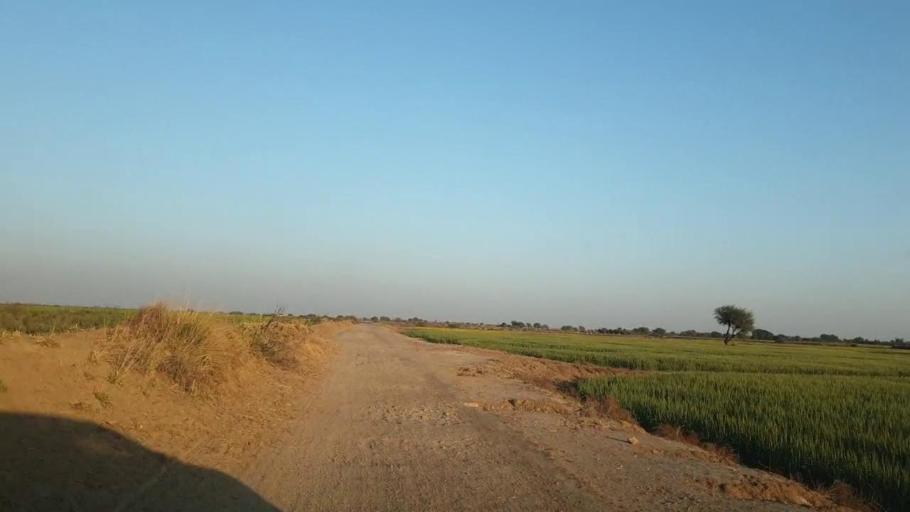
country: PK
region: Sindh
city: Mirpur Khas
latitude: 25.7081
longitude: 69.0484
